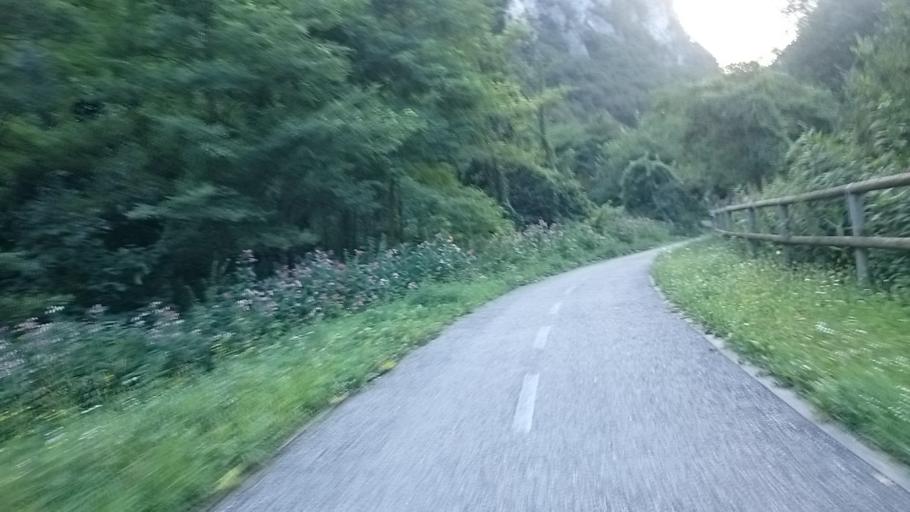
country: IT
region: Veneto
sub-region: Provincia di Vicenza
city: Enego
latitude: 45.9575
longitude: 11.7088
